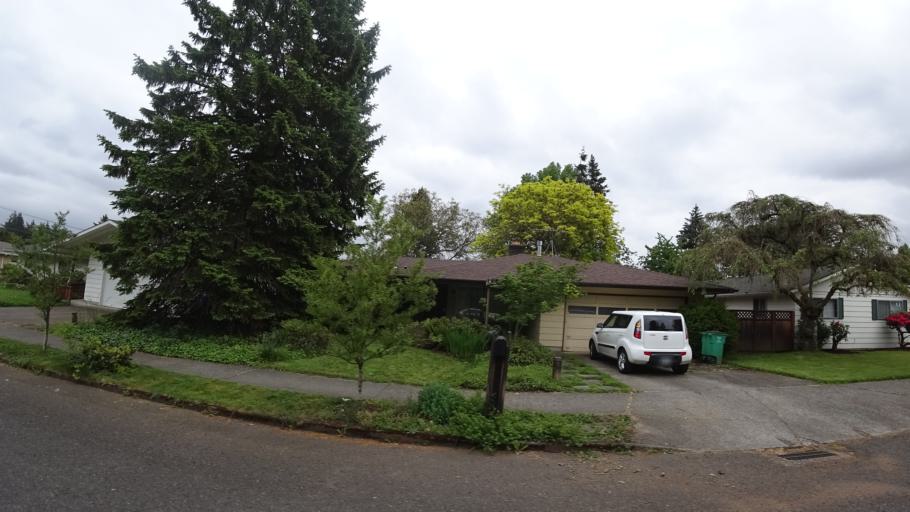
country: US
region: Oregon
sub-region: Multnomah County
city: Lents
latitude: 45.5085
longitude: -122.5227
